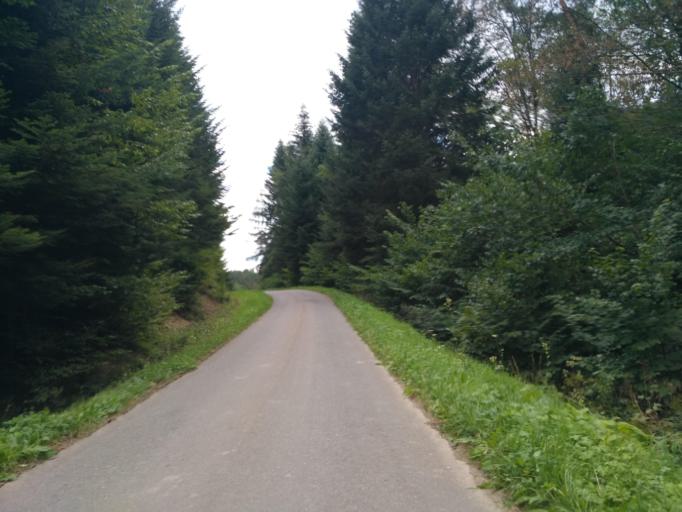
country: PL
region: Subcarpathian Voivodeship
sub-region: Powiat rzeszowski
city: Dynow
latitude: 49.7639
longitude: 22.2749
